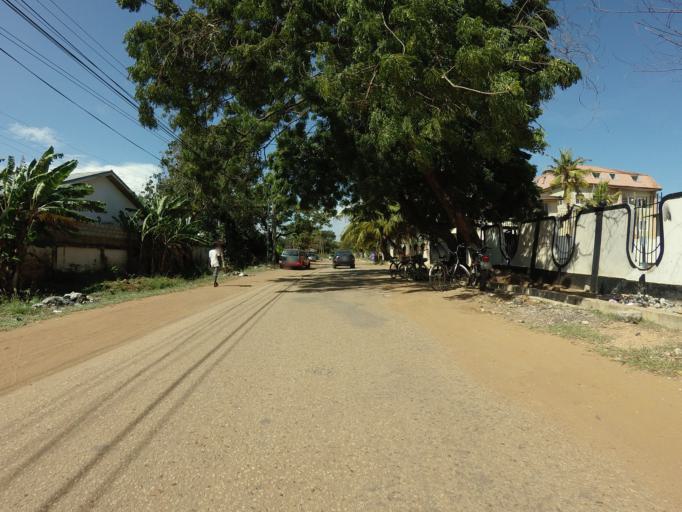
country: GH
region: Greater Accra
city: Accra
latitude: 5.5696
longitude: -0.1728
